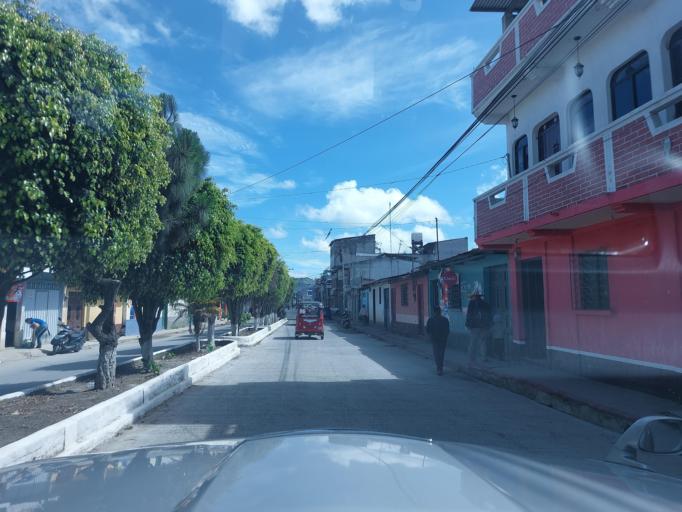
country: GT
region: Chimaltenango
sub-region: Municipio de San Juan Comalapa
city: Comalapa
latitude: 14.7346
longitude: -90.8869
